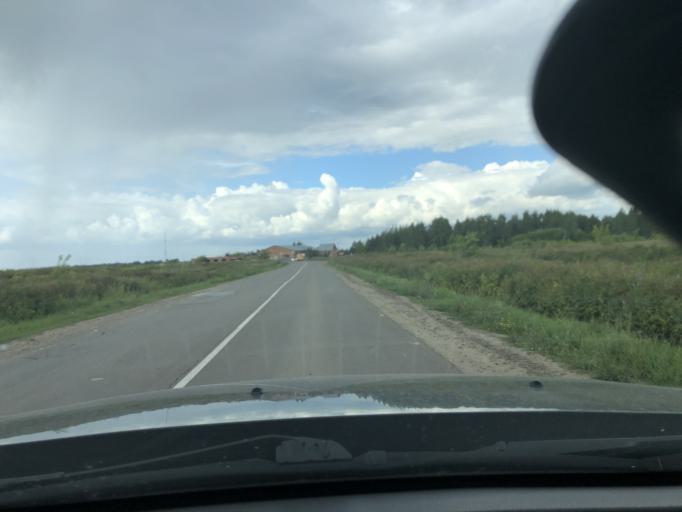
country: RU
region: Tula
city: Kamenetskiy
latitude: 54.0149
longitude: 38.2517
